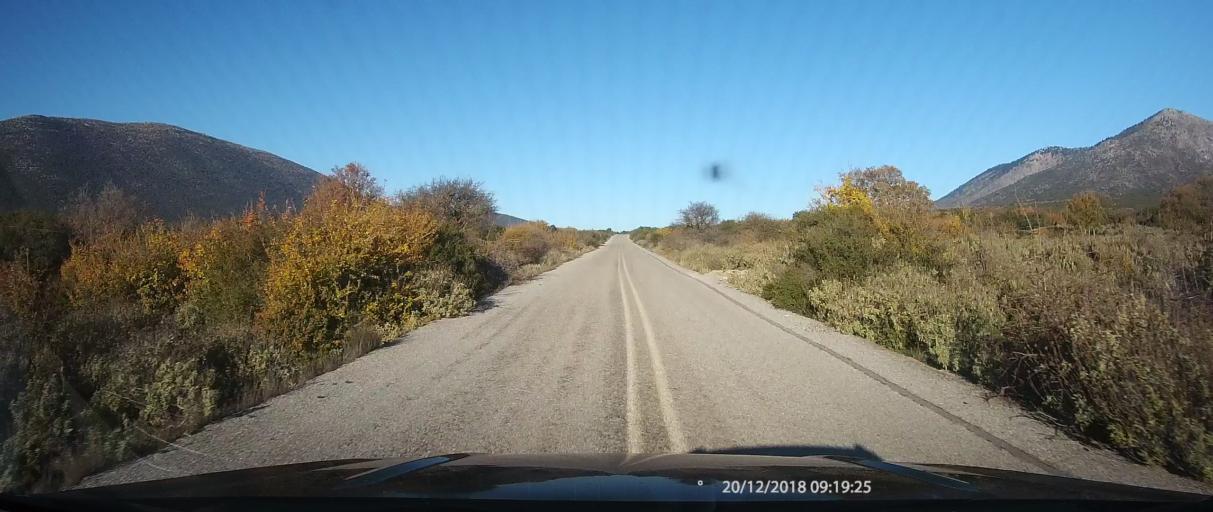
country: GR
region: Peloponnese
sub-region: Nomos Lakonias
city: Molaoi
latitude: 36.9186
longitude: 22.9404
